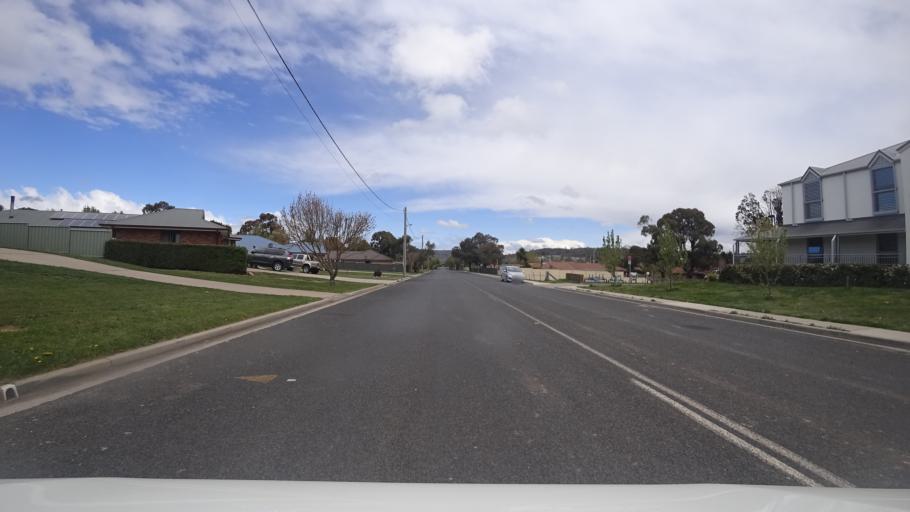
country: AU
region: New South Wales
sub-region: Oberon
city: Oberon
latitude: -33.7017
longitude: 149.8727
